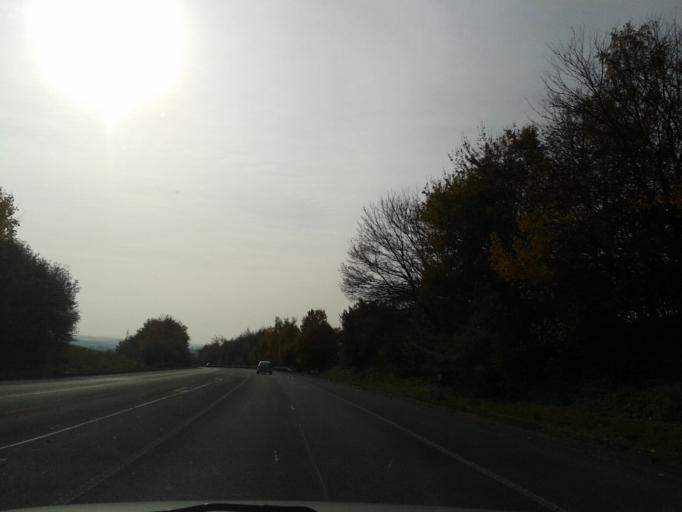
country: DE
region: North Rhine-Westphalia
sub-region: Regierungsbezirk Arnsberg
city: Ruthen
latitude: 51.5152
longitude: 8.4529
